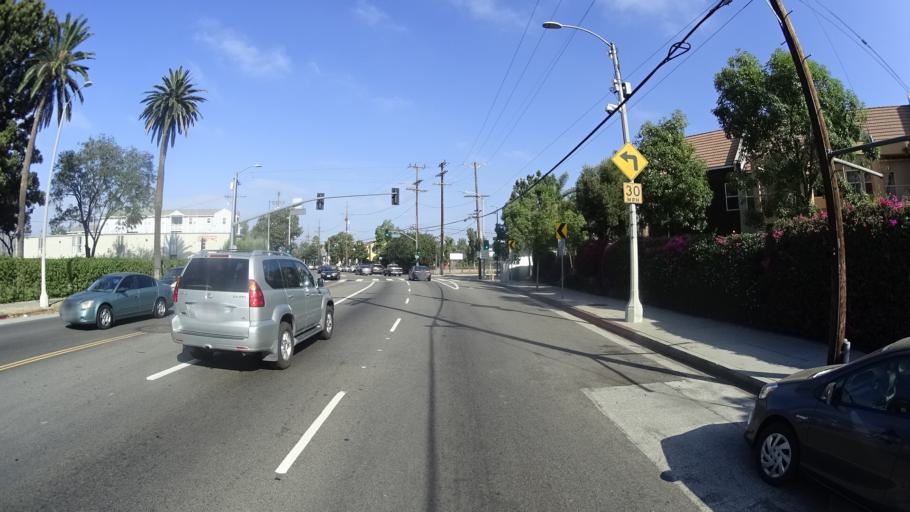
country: US
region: California
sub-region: Los Angeles County
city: Los Angeles
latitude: 34.0326
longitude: -118.2859
